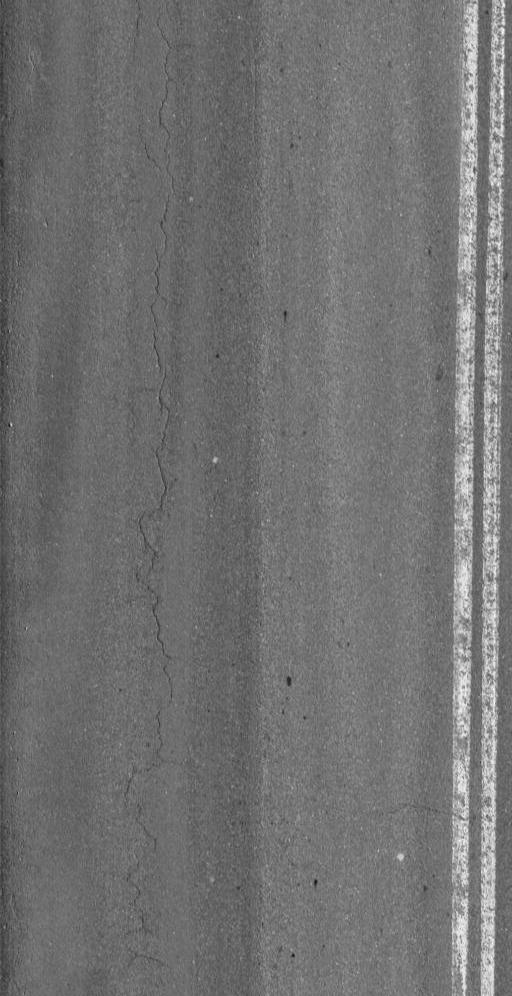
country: US
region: Vermont
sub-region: Windham County
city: Bellows Falls
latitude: 43.1225
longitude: -72.4691
